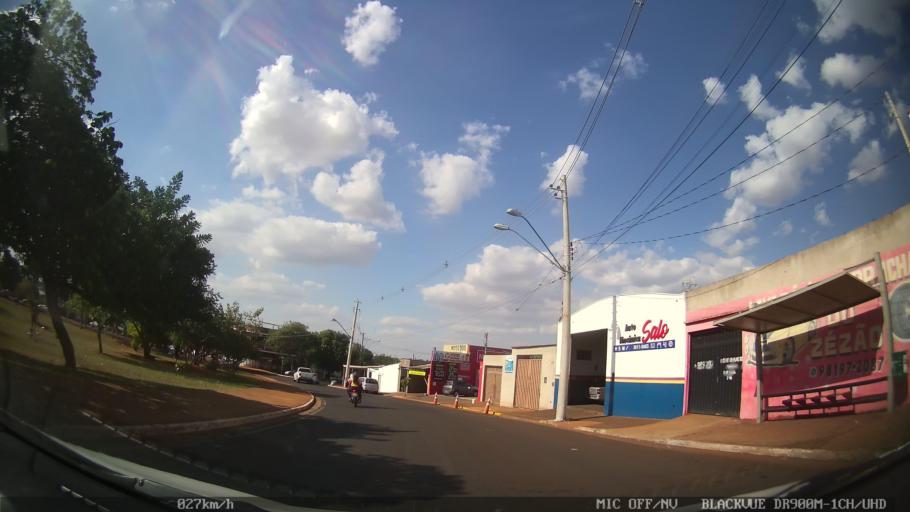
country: BR
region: Sao Paulo
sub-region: Ribeirao Preto
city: Ribeirao Preto
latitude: -21.1995
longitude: -47.8385
